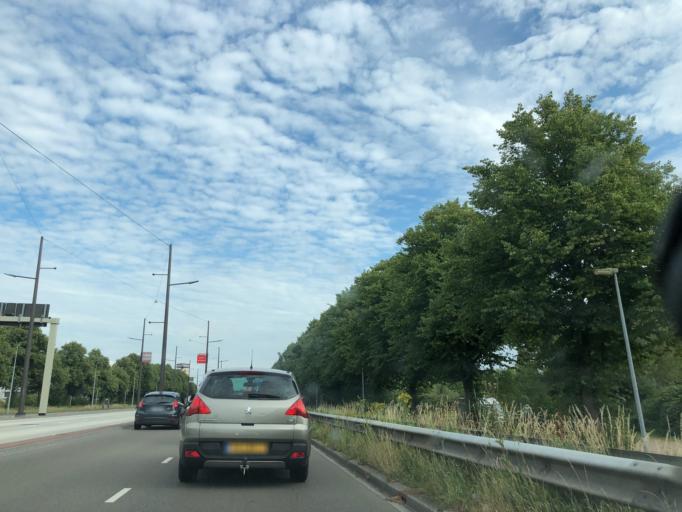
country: NL
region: Groningen
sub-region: Gemeente Groningen
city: Oosterpark
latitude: 53.2144
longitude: 6.5836
